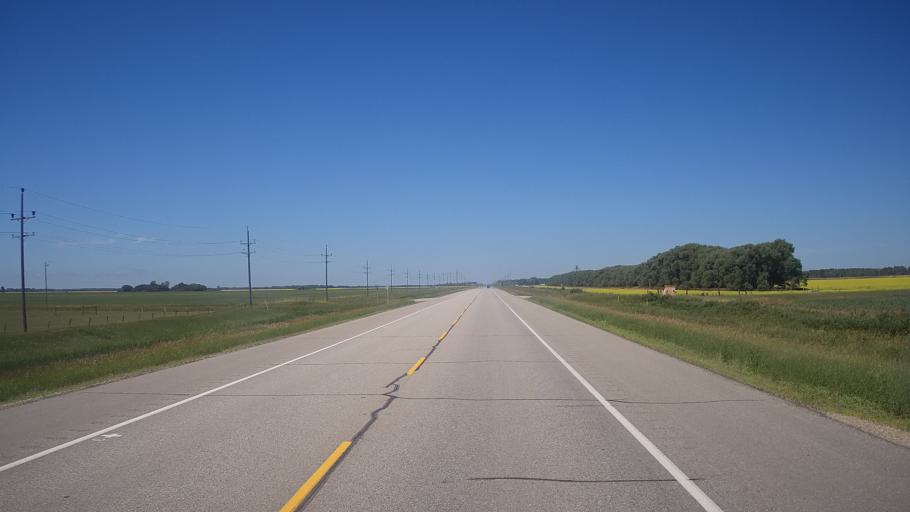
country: CA
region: Manitoba
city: Neepawa
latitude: 50.2257
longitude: -99.0634
